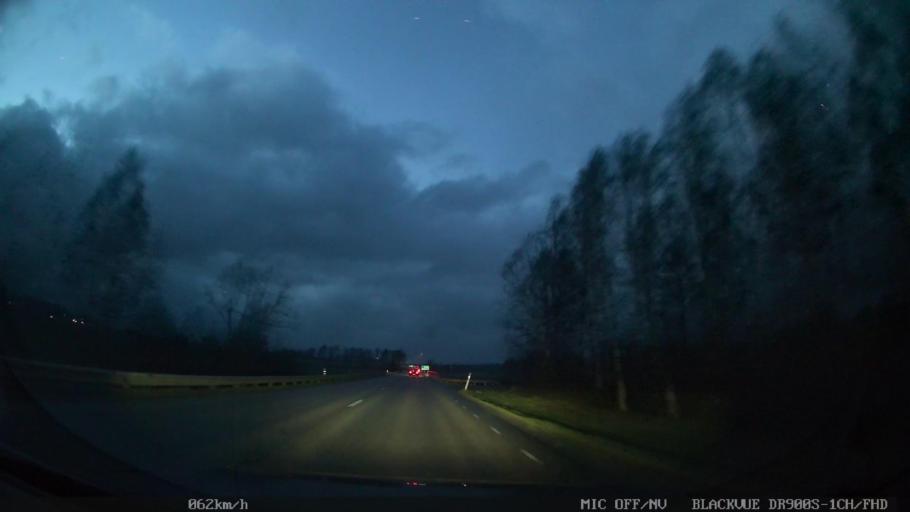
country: SE
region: Skane
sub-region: Hassleholms Kommun
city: Hassleholm
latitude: 56.1738
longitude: 13.7564
